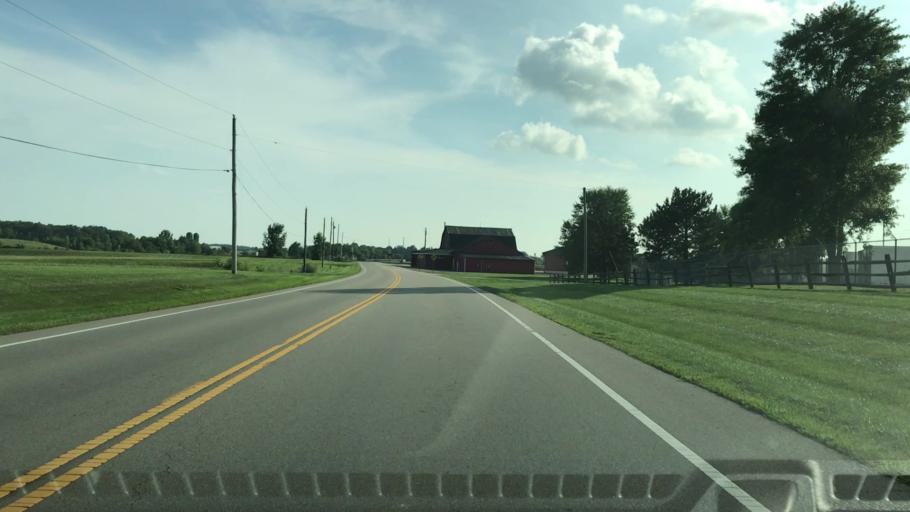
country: US
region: Ohio
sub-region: Union County
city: Marysville
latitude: 40.2047
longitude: -83.3150
